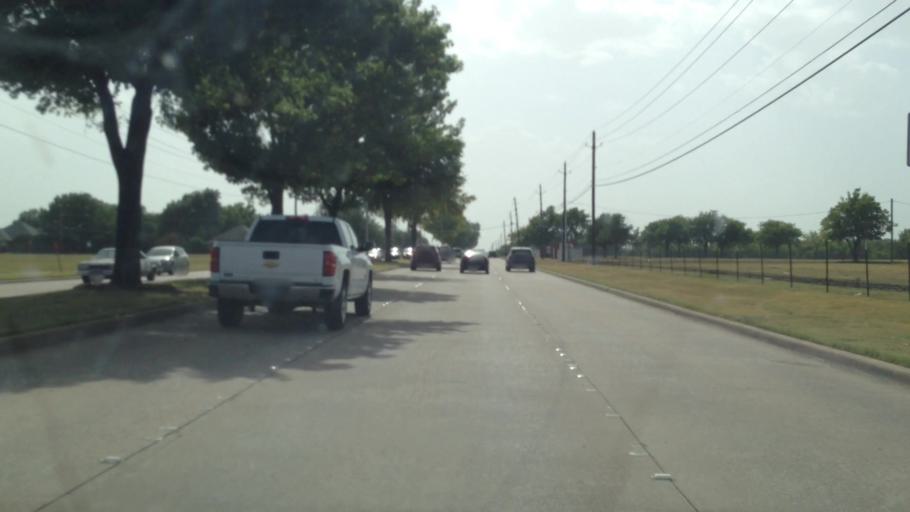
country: US
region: Texas
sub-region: Collin County
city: Plano
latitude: 33.0265
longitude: -96.7179
